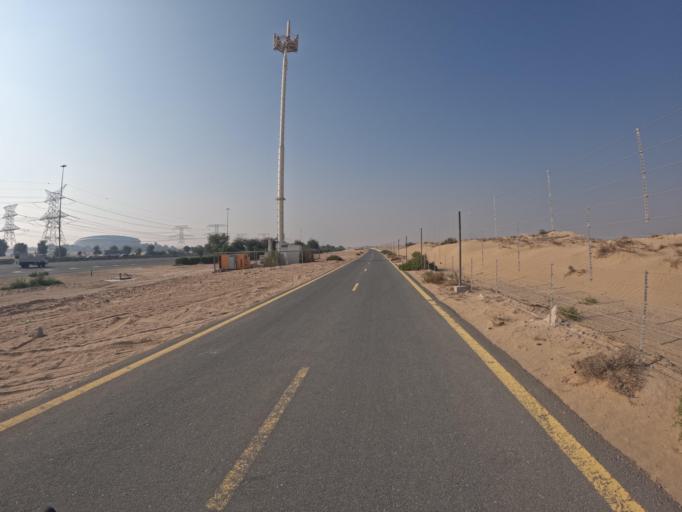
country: AE
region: Dubai
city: Dubai
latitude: 25.0586
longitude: 55.3189
